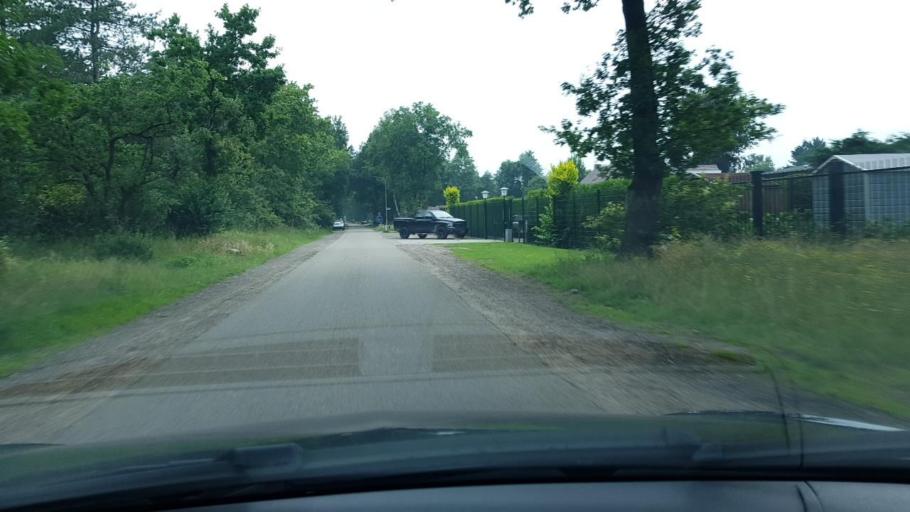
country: NL
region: Gelderland
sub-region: Gemeente Harderwijk
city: Harderwijk
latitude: 52.3208
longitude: 5.6357
